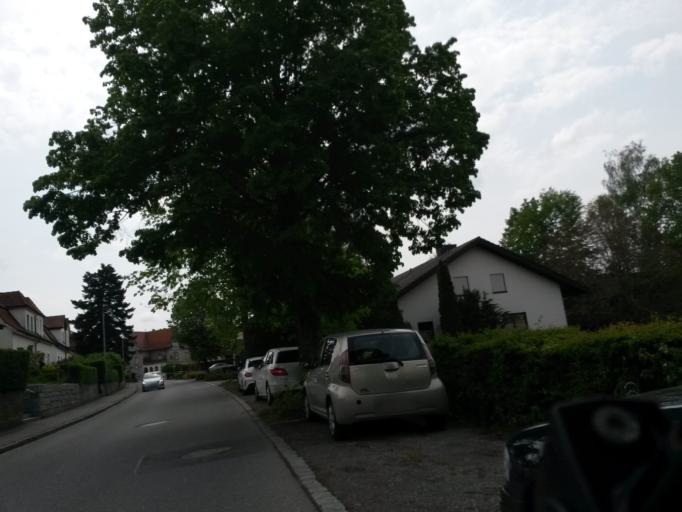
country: DE
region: Baden-Wuerttemberg
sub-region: Tuebingen Region
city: Bad Waldsee
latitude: 47.9268
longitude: 9.7479
